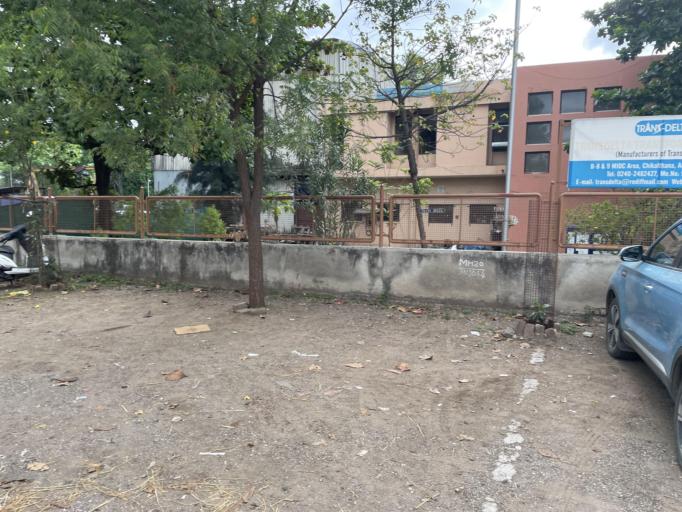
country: IN
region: Maharashtra
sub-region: Aurangabad Division
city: Aurangabad
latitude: 19.8815
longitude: 75.3879
